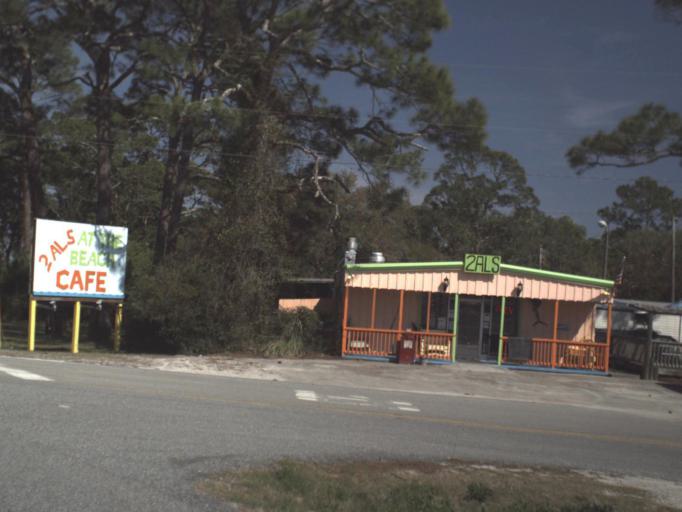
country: US
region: Florida
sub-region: Franklin County
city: Carrabelle
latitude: 29.8331
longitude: -84.6847
